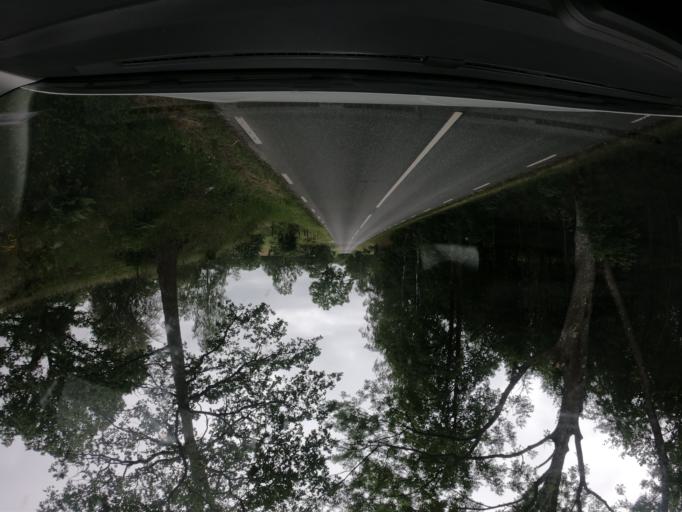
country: SE
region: Skane
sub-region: Hoors Kommun
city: Hoeoer
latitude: 55.9766
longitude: 13.5178
